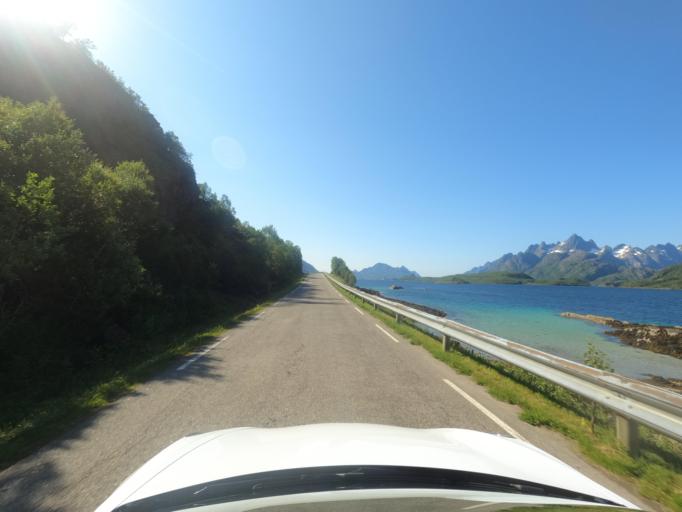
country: NO
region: Nordland
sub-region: Hadsel
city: Stokmarknes
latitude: 68.3751
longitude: 15.0785
